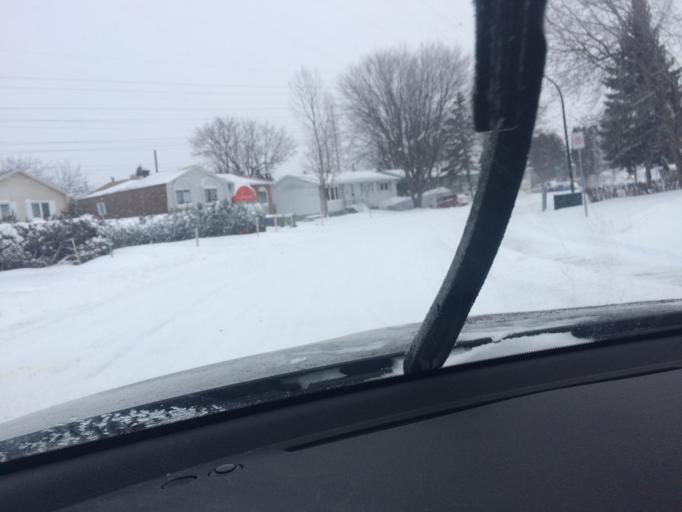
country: CA
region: Quebec
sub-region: Monteregie
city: Brossard
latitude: 45.4694
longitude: -73.4567
